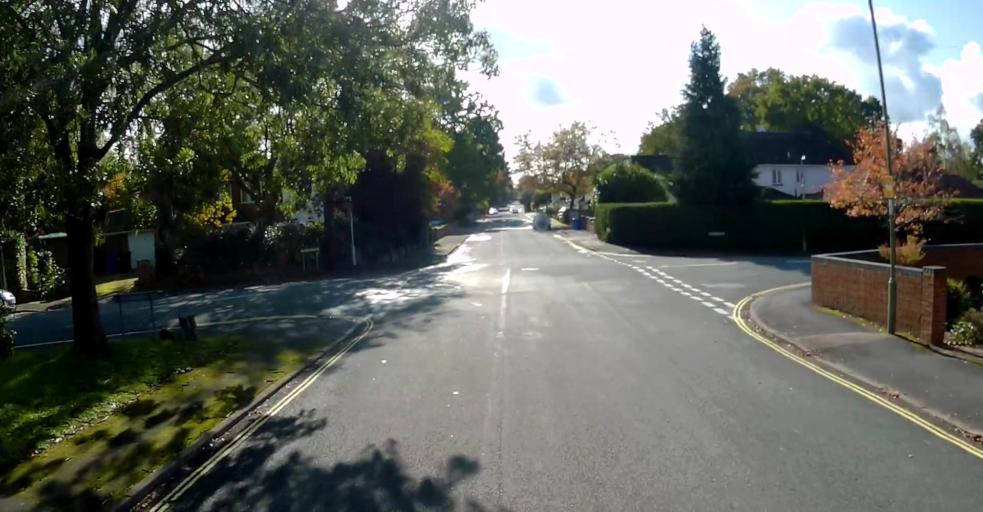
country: GB
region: England
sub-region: Hampshire
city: Farnborough
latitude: 51.2909
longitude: -0.7513
